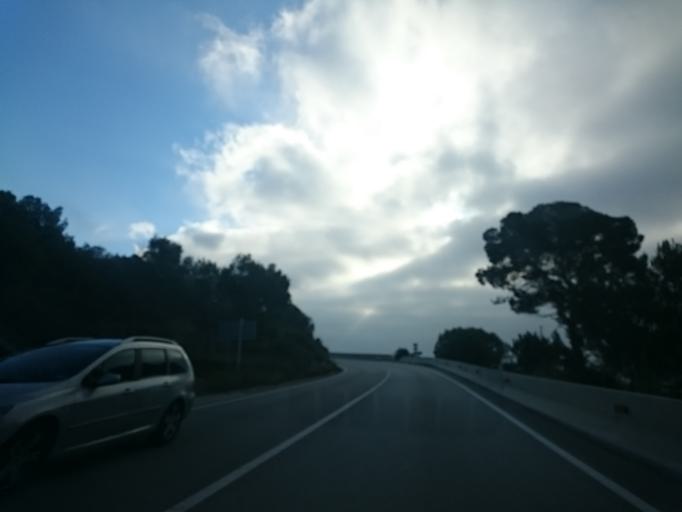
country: ES
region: Catalonia
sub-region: Provincia de Barcelona
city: Castelldefels
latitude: 41.2616
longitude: 1.9229
